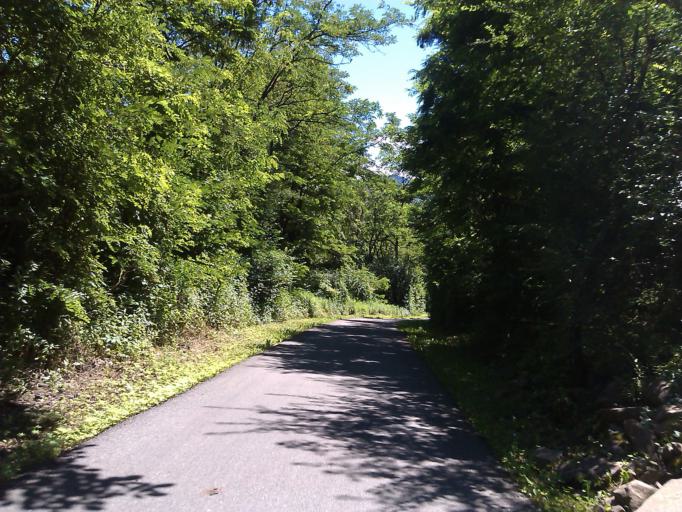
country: IT
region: Trentino-Alto Adige
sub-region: Bolzano
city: San Giacomo
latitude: 46.4464
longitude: 11.3081
